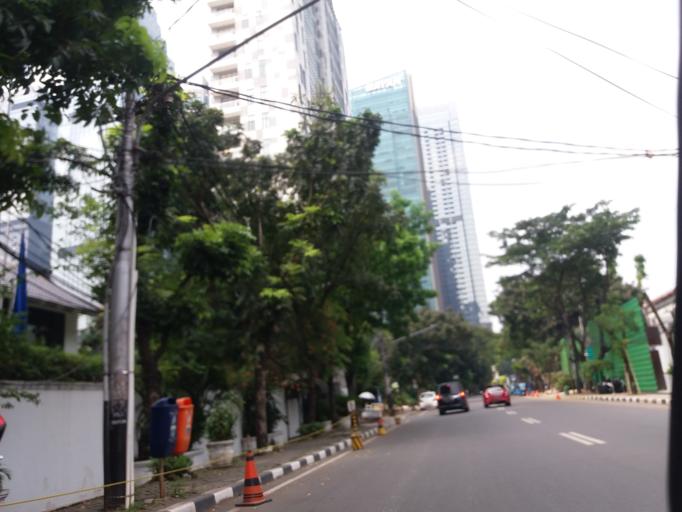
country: ID
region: Jakarta Raya
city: Jakarta
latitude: -6.2293
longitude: 106.8034
